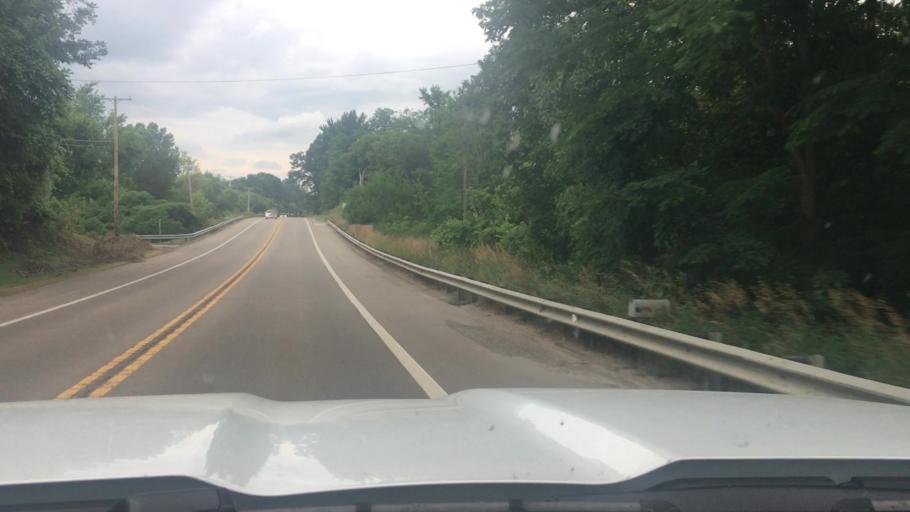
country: US
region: Michigan
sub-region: Ionia County
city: Ionia
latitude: 43.0016
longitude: -84.9510
